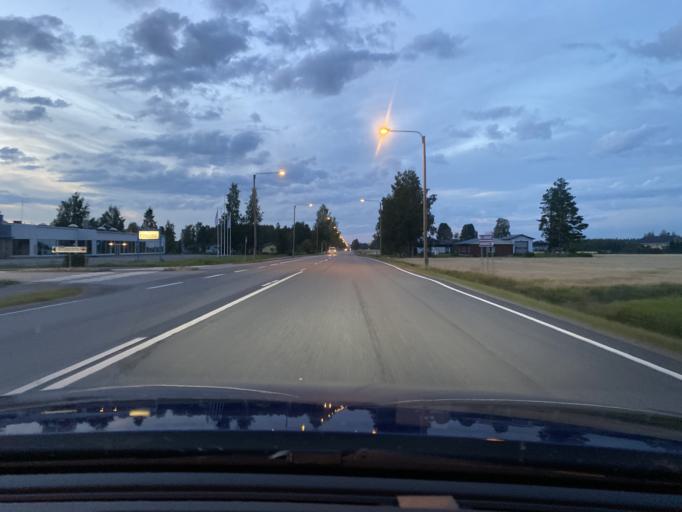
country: FI
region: Southern Ostrobothnia
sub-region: Suupohja
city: Kauhajoki
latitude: 62.4299
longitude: 22.2038
